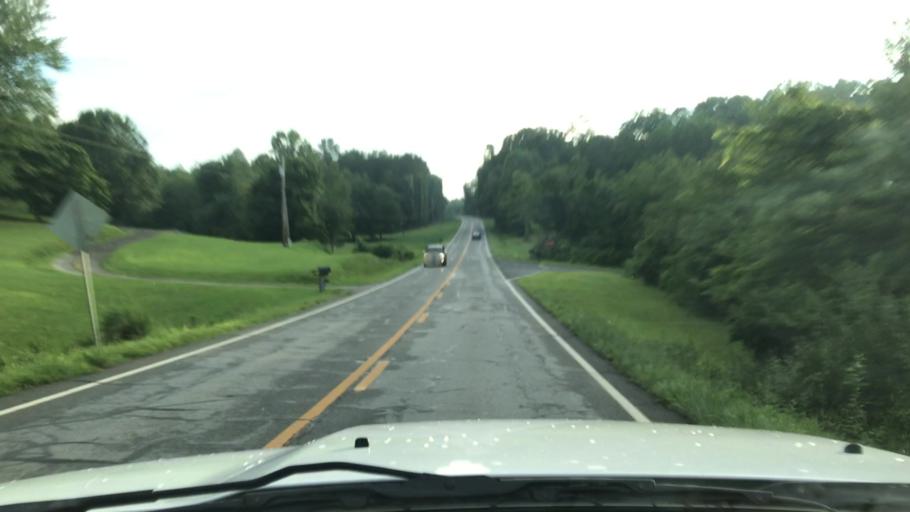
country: US
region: Georgia
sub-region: Fannin County
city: Blue Ridge
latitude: 34.9823
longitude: -84.1906
